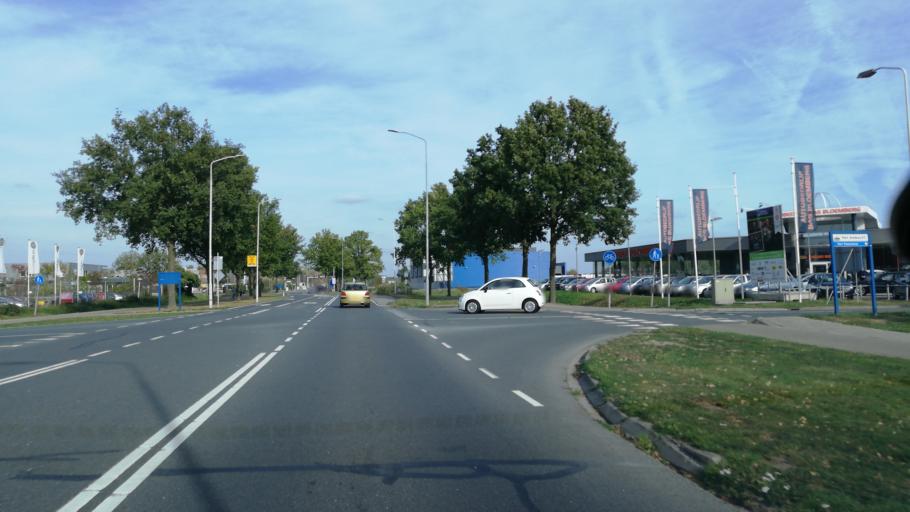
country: NL
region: Gelderland
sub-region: Gemeente Westervoort
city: Westervoort
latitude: 51.9578
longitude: 5.9825
